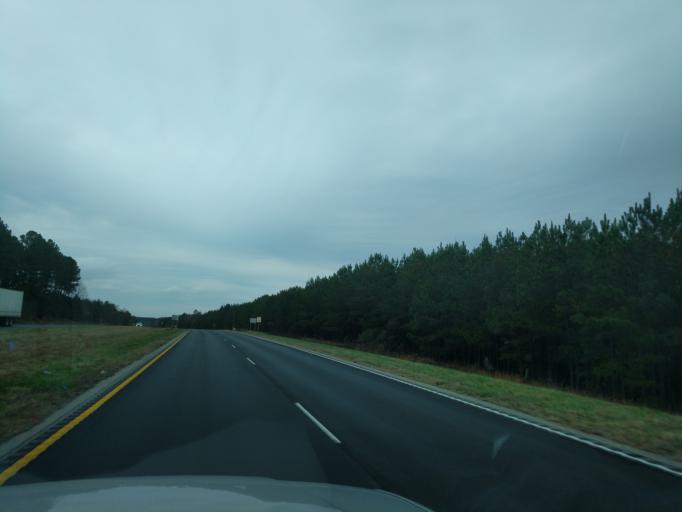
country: US
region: South Carolina
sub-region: Laurens County
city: Clinton
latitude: 34.3801
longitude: -81.9507
